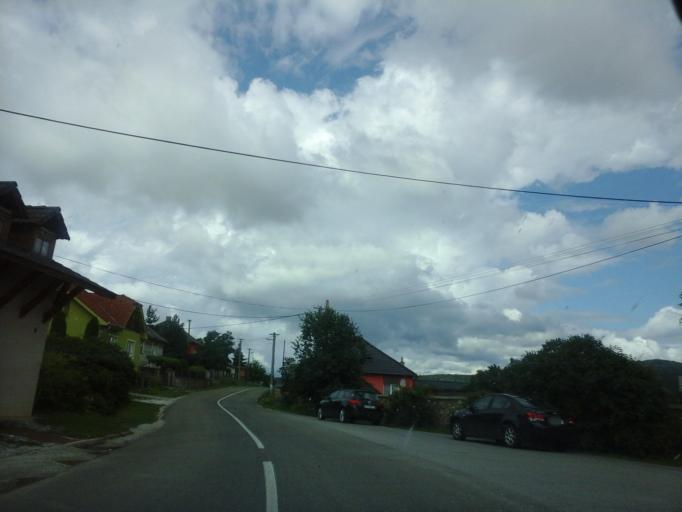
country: SK
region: Kosicky
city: Roznava
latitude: 48.4968
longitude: 20.4369
